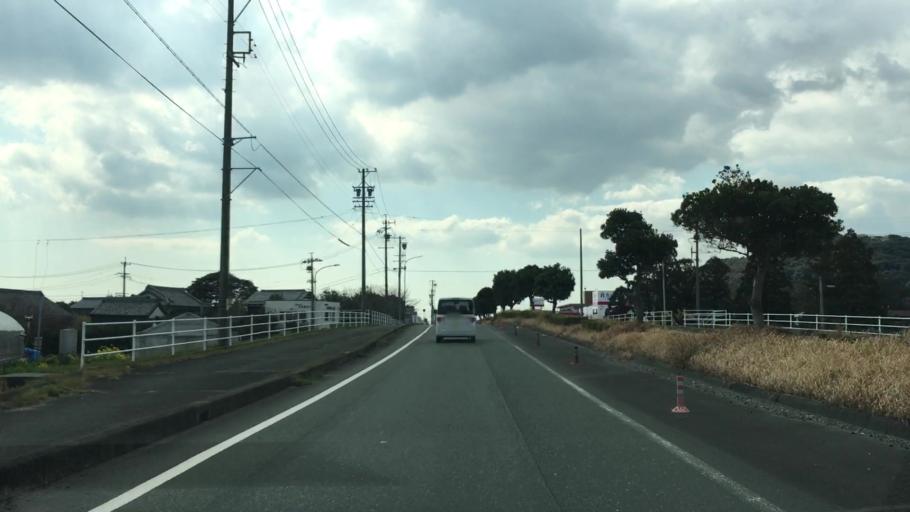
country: JP
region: Aichi
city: Kozakai-cho
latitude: 34.8182
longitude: 137.3228
